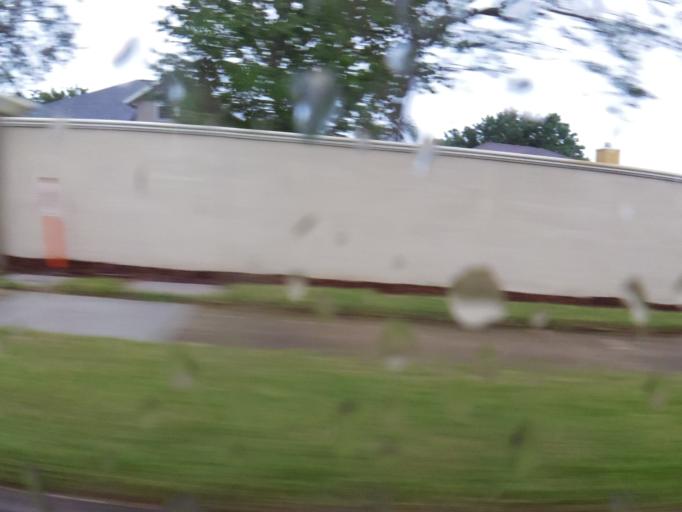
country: US
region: Florida
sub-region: Saint Johns County
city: Ponte Vedra Beach
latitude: 30.2626
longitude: -81.3945
